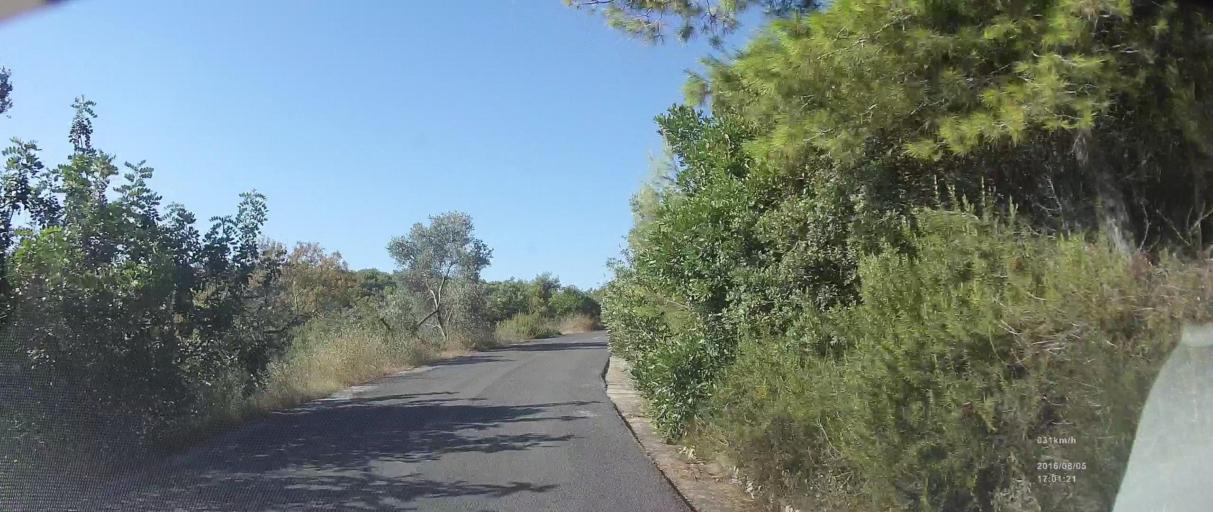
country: HR
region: Dubrovacko-Neretvanska
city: Blato
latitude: 42.7830
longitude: 17.3674
